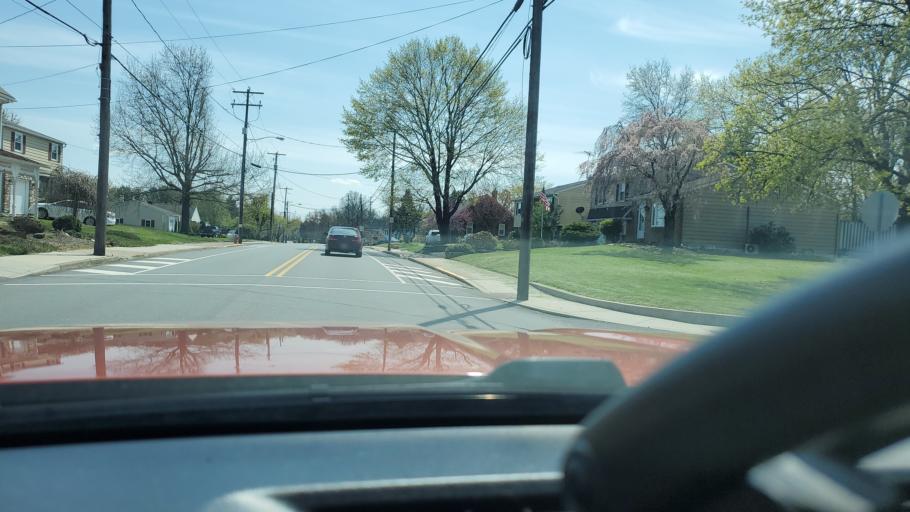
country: US
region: Pennsylvania
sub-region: Montgomery County
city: Red Hill
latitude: 40.3689
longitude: -75.4831
